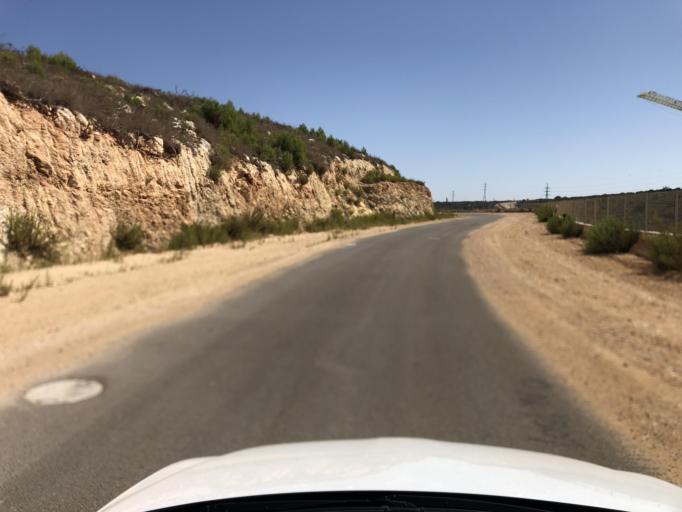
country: PS
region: West Bank
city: Kafr Thulth
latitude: 32.1651
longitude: 35.0286
